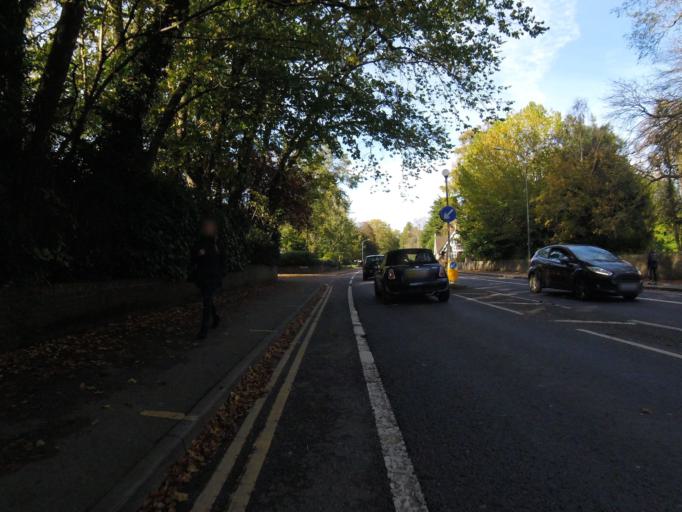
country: GB
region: England
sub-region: Brighton and Hove
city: Hove
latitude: 50.8465
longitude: -0.1520
